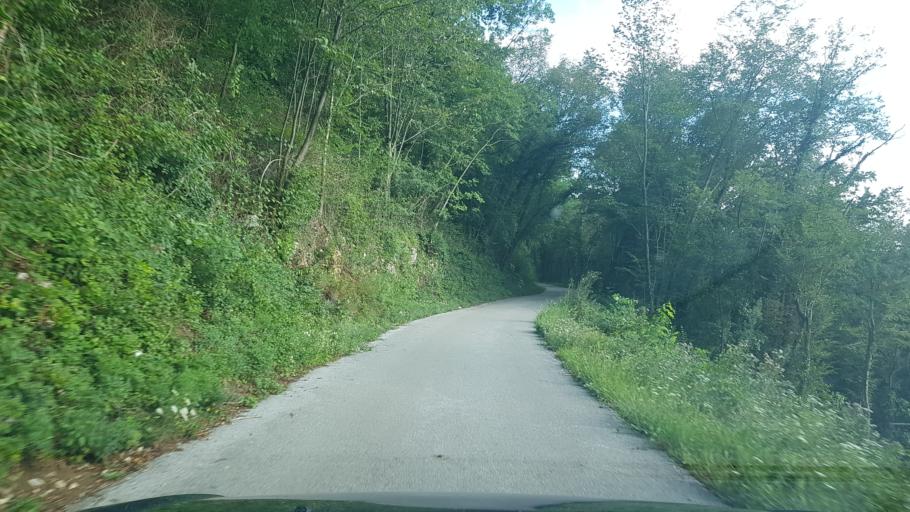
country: SI
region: Kanal
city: Deskle
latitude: 46.0278
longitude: 13.6097
